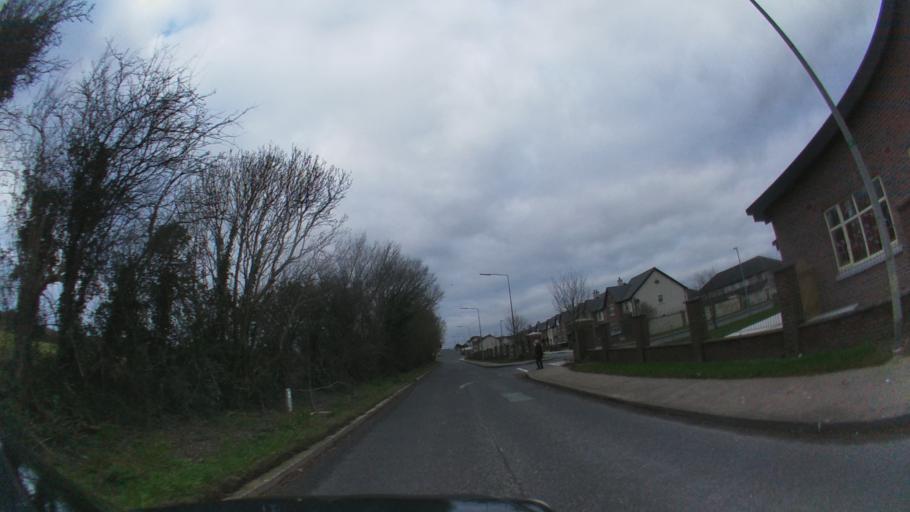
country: IE
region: Leinster
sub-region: Lu
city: Drogheda
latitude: 53.6986
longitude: -6.3670
